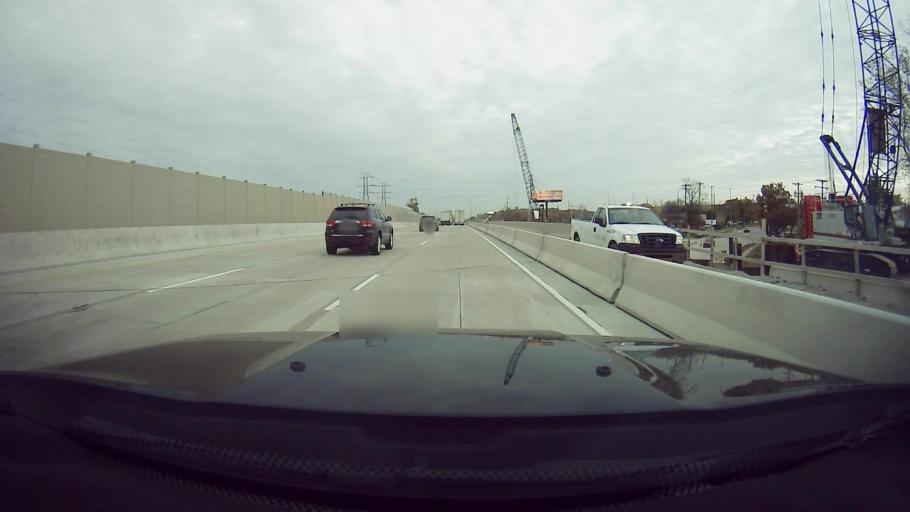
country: US
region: Michigan
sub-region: Wayne County
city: Southgate
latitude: 42.2277
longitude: -83.2127
